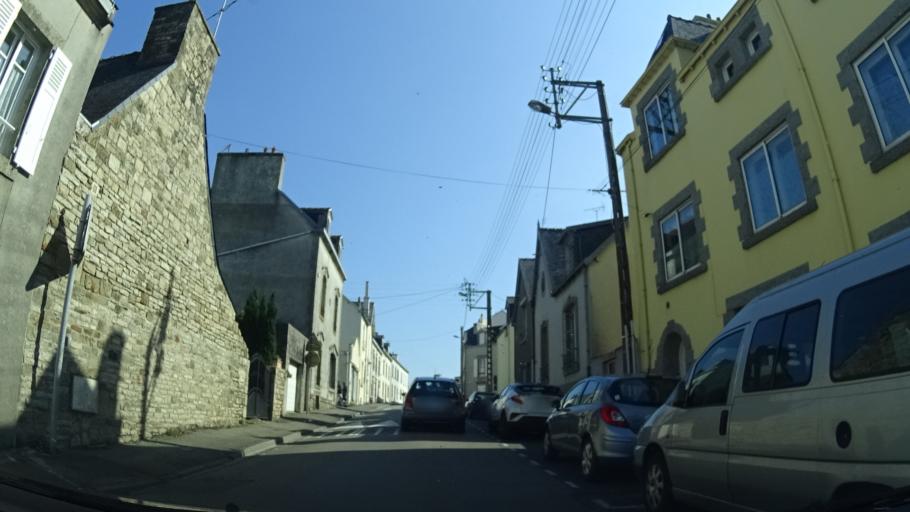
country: FR
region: Brittany
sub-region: Departement du Finistere
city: Douarnenez
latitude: 48.0932
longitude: -4.3393
